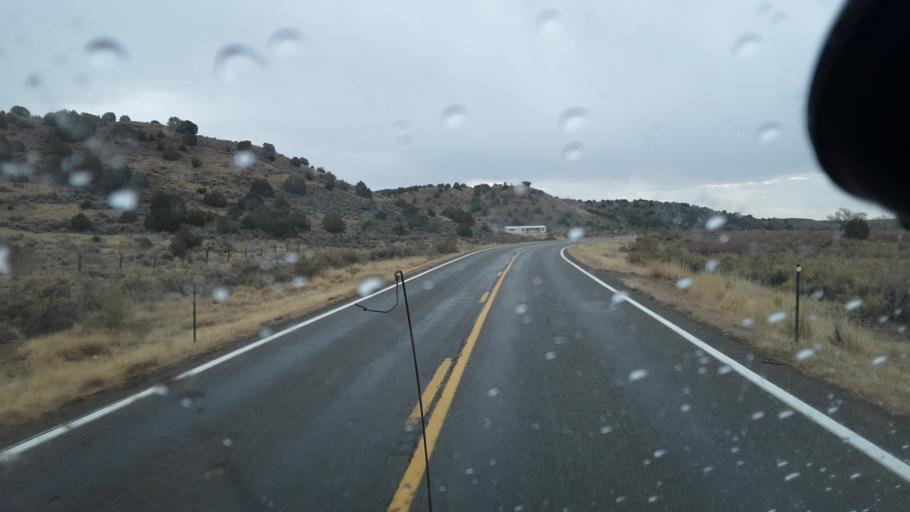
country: US
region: New Mexico
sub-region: San Juan County
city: Spencerville
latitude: 37.0087
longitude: -108.1820
